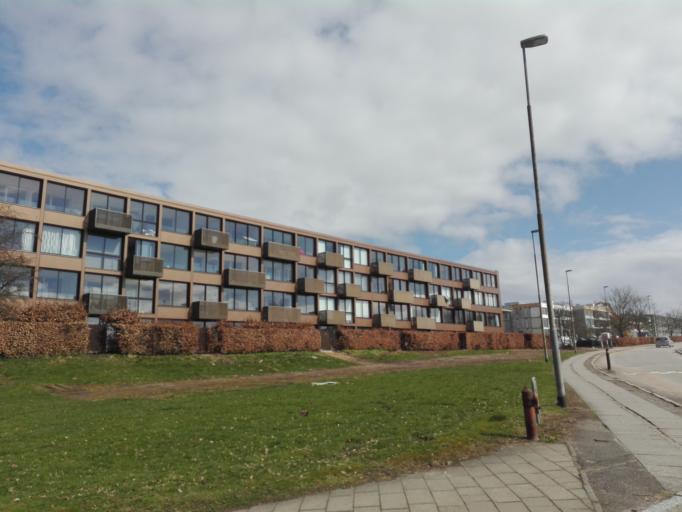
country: DK
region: Central Jutland
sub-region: Arhus Kommune
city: Stavtrup
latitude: 56.1131
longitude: 10.1435
